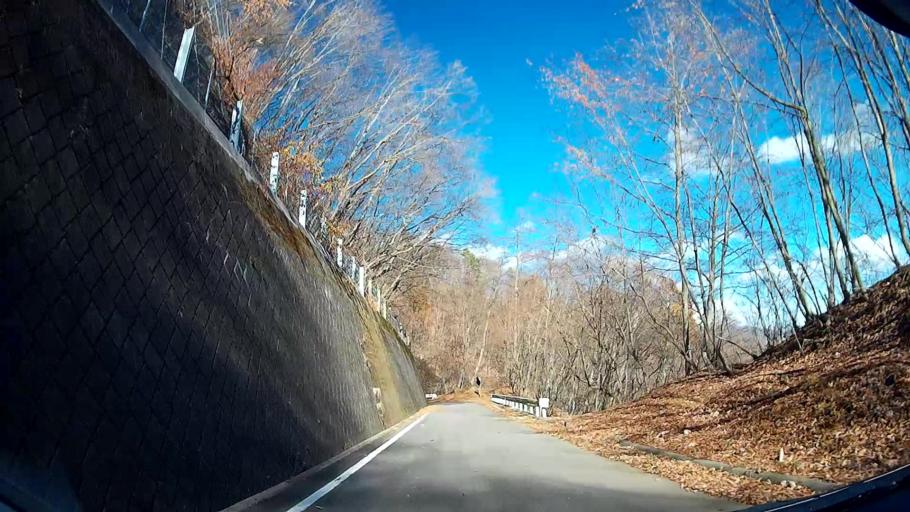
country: JP
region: Yamanashi
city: Otsuki
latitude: 35.7310
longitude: 138.9469
